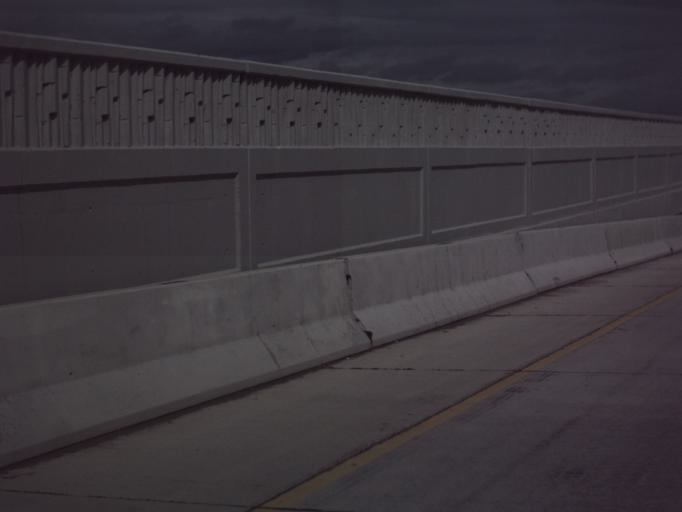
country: US
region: Utah
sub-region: Salt Lake County
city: West Jordan
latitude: 40.6071
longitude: -111.9763
